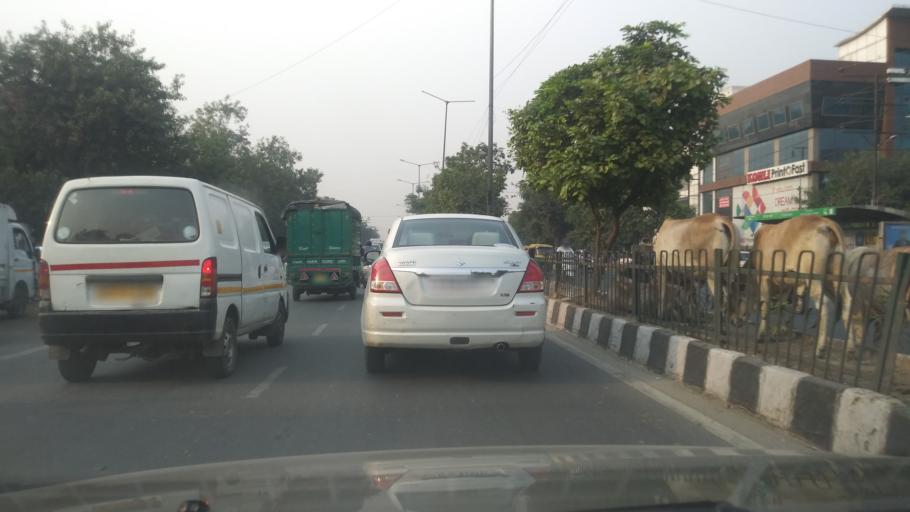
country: IN
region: Uttar Pradesh
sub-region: Gautam Buddha Nagar
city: Noida
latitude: 28.5338
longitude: 77.2686
